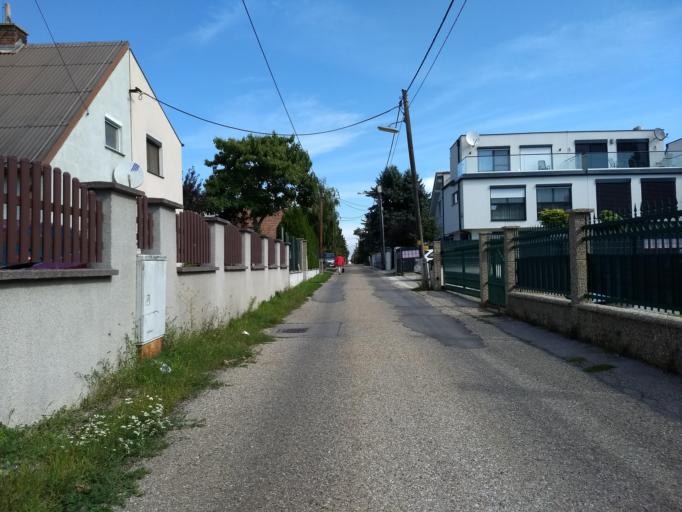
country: AT
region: Lower Austria
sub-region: Politischer Bezirk Ganserndorf
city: Gross-Enzersdorf
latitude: 48.2270
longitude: 16.4921
